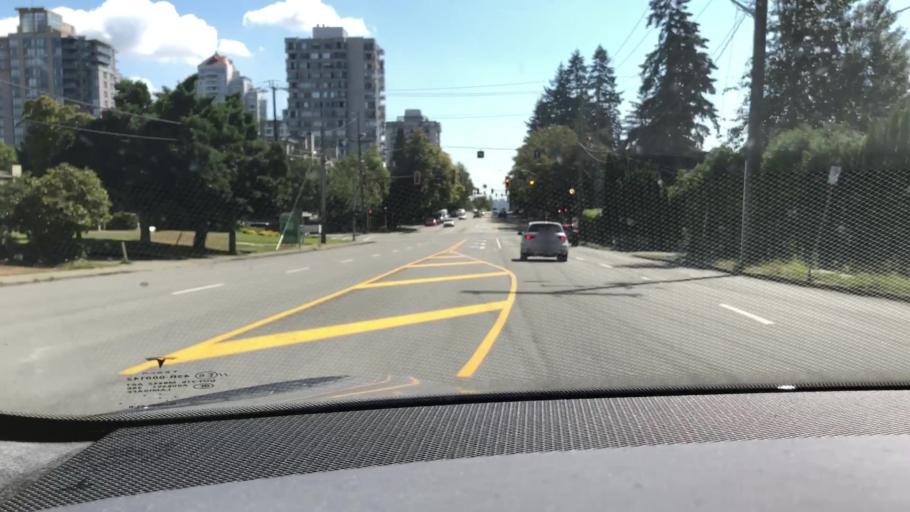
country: CA
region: British Columbia
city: New Westminster
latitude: 49.2147
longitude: -122.9285
